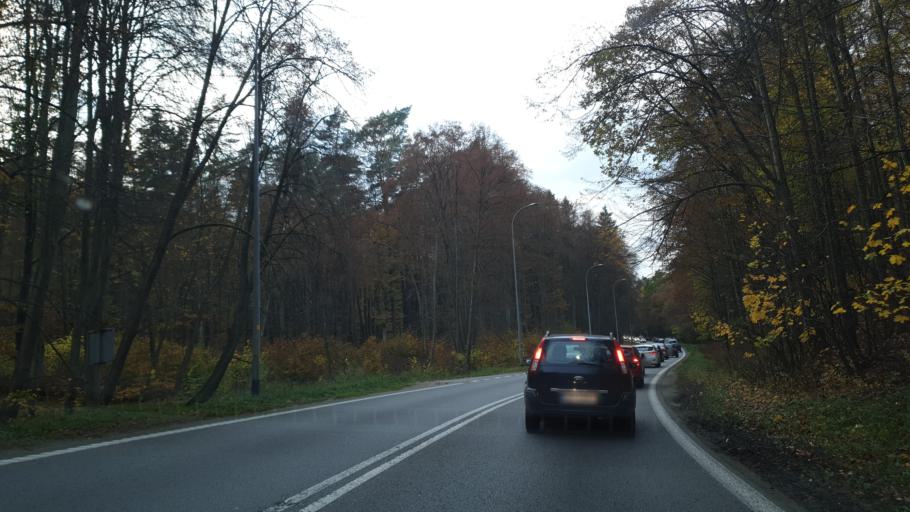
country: PL
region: Pomeranian Voivodeship
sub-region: Sopot
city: Sopot
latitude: 54.4212
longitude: 18.5176
